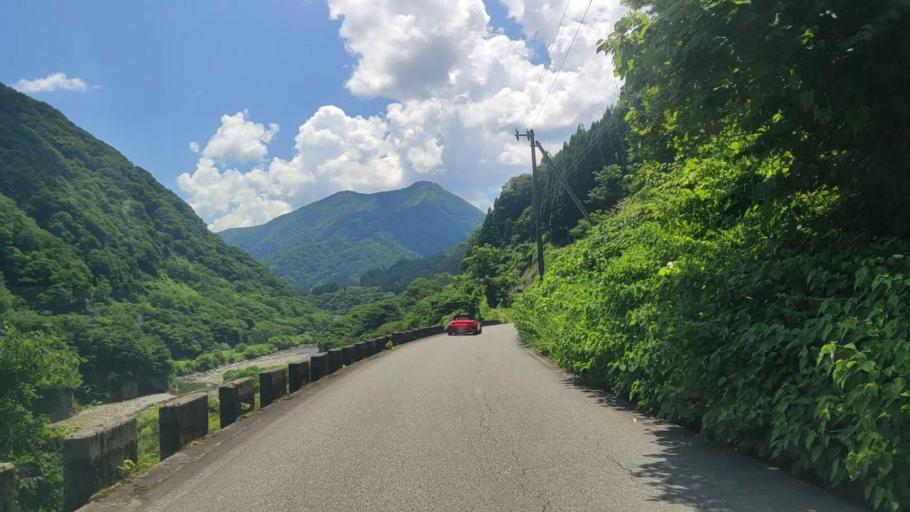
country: JP
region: Fukui
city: Ono
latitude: 35.8911
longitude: 136.5066
